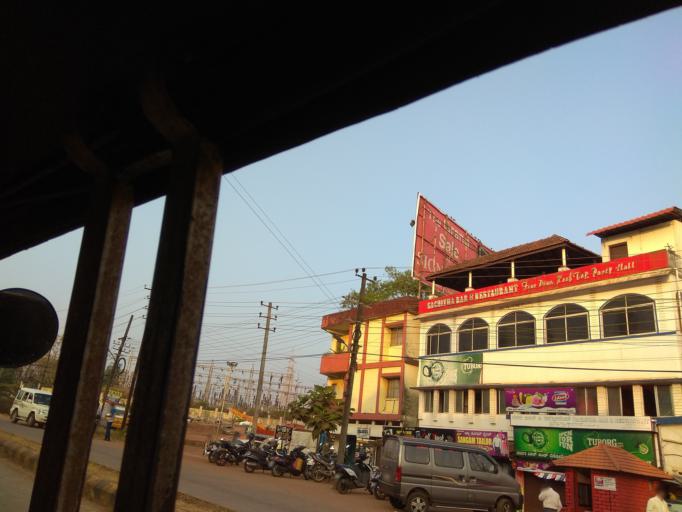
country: IN
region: Karnataka
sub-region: Dakshina Kannada
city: Mangalore
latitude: 12.9247
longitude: 74.8587
